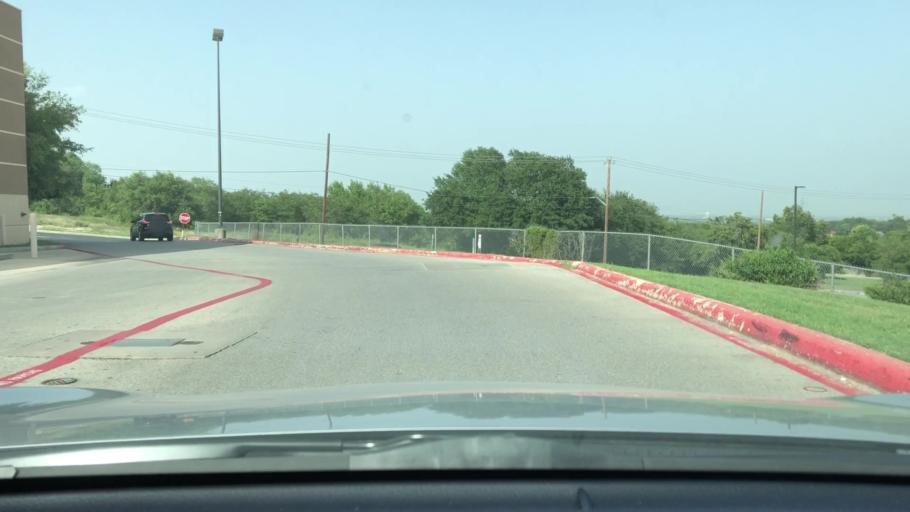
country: US
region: Texas
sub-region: Bexar County
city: Live Oak
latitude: 29.5631
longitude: -98.3262
